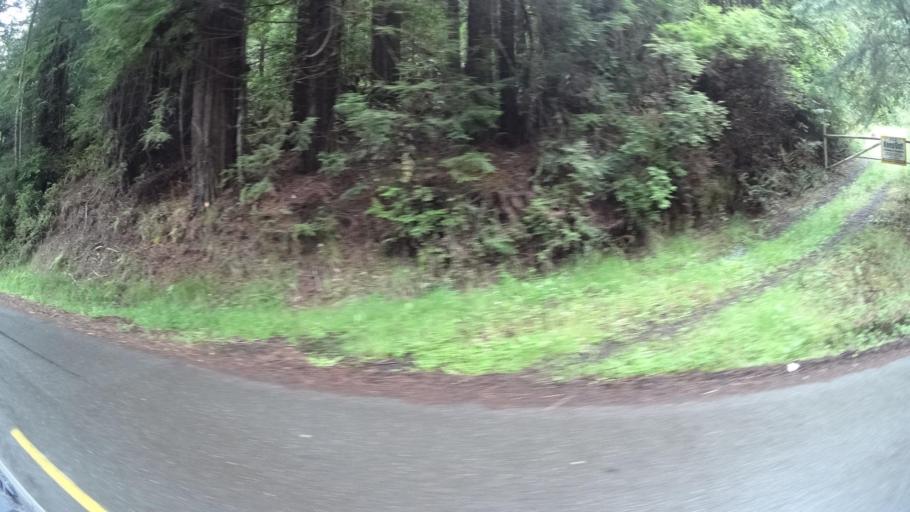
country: US
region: California
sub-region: Humboldt County
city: Bayside
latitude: 40.8251
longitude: -124.0350
